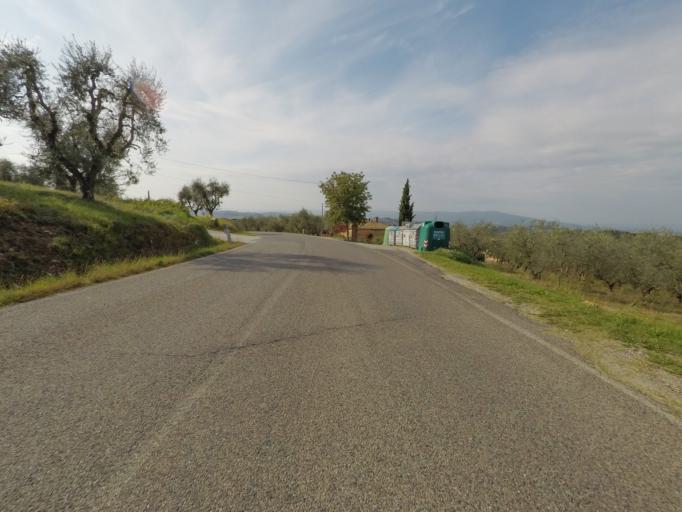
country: IT
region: Tuscany
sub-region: Provincia di Siena
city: Belverde
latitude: 43.3919
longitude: 11.3456
